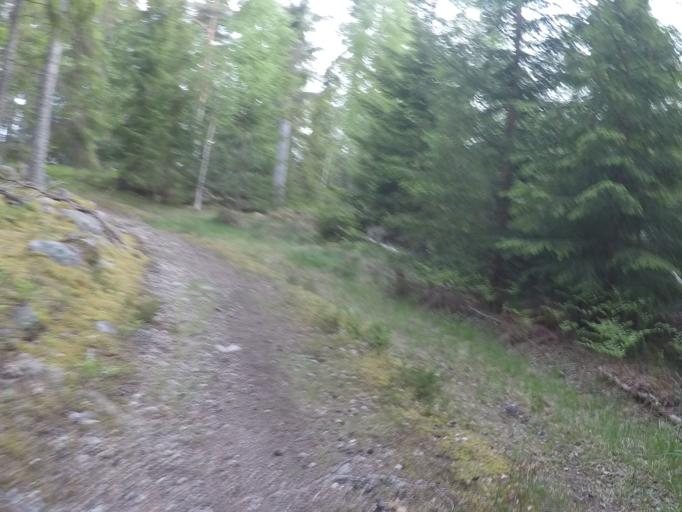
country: SE
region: Soedermanland
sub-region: Eskilstuna Kommun
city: Kvicksund
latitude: 59.4084
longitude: 16.3027
